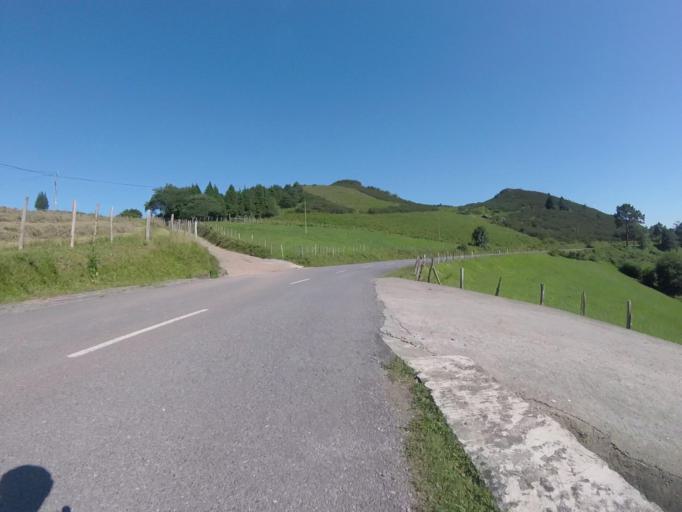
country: ES
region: Basque Country
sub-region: Provincia de Guipuzcoa
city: Irun
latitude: 43.3013
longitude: -1.8216
